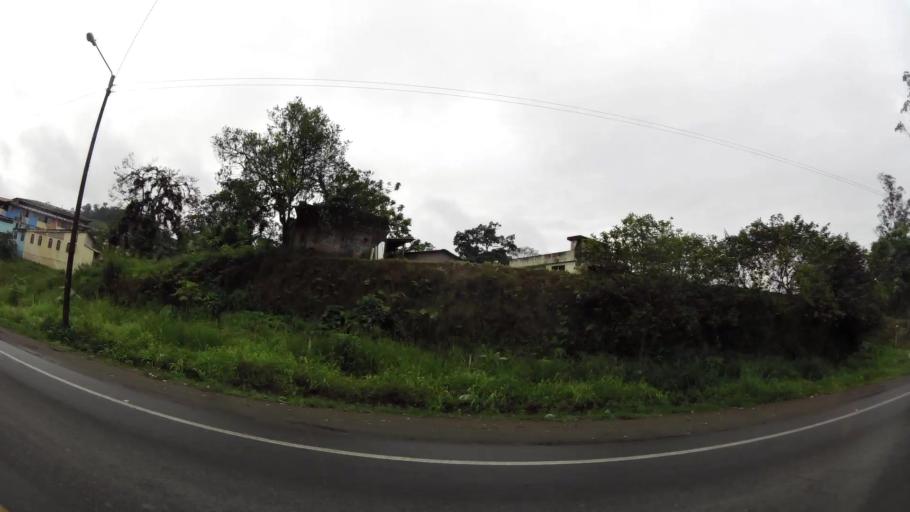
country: EC
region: Santo Domingo de los Tsachilas
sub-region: Canton Santo Domingo de los Colorados
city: Santo Domingo de los Colorados
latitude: -0.2480
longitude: -79.2012
